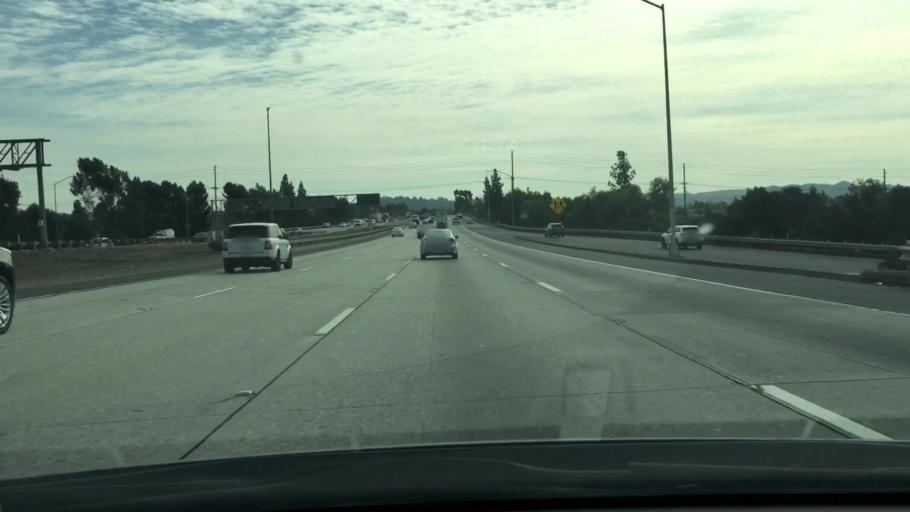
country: US
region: California
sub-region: Los Angeles County
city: San Dimas
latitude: 34.1160
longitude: -117.8244
